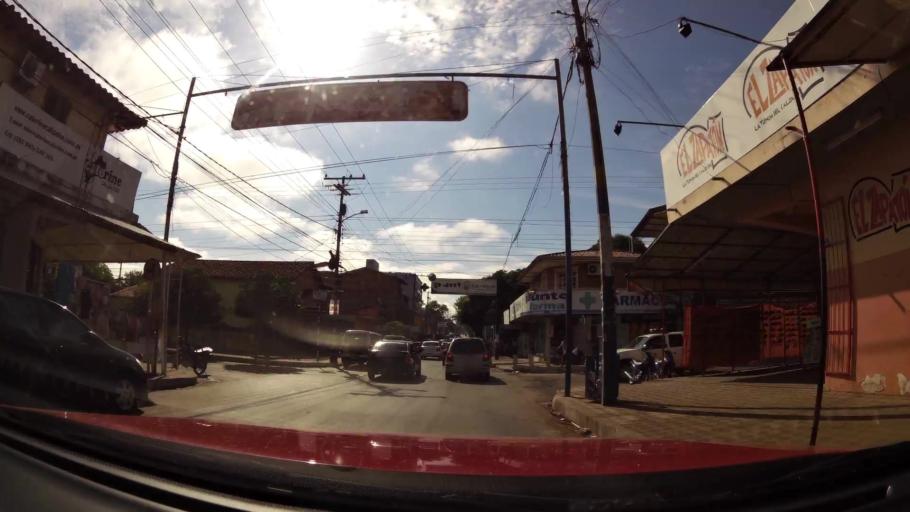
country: PY
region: Central
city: San Lorenzo
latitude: -25.2683
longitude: -57.4888
